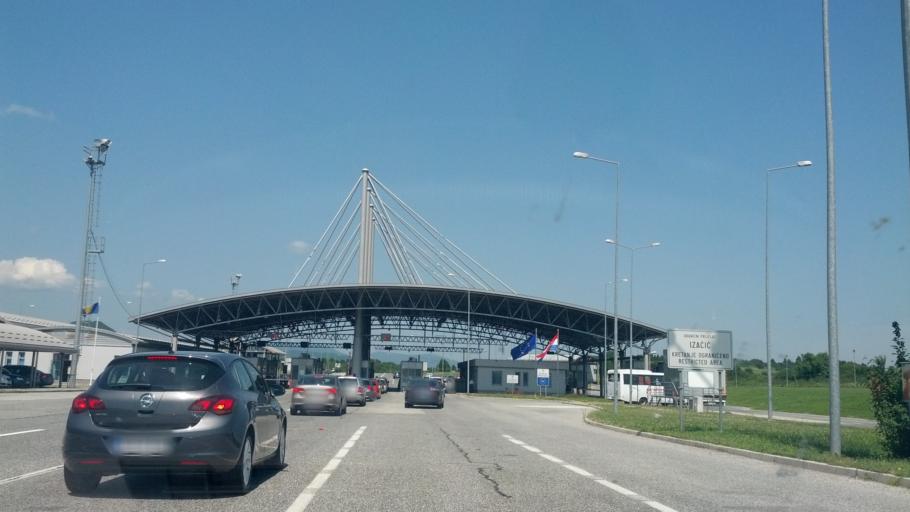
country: BA
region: Federation of Bosnia and Herzegovina
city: Izacic
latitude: 44.8744
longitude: 15.7652
